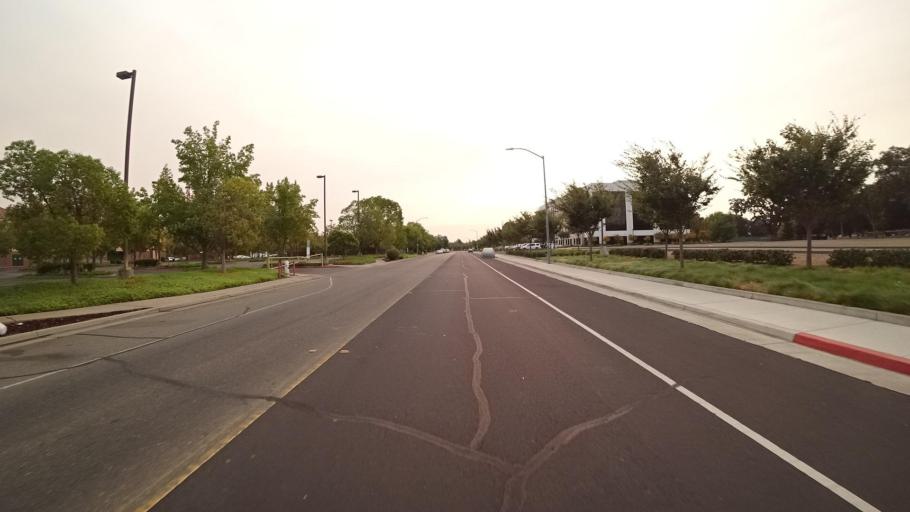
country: US
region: California
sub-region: Sacramento County
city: Laguna
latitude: 38.4170
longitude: -121.4051
